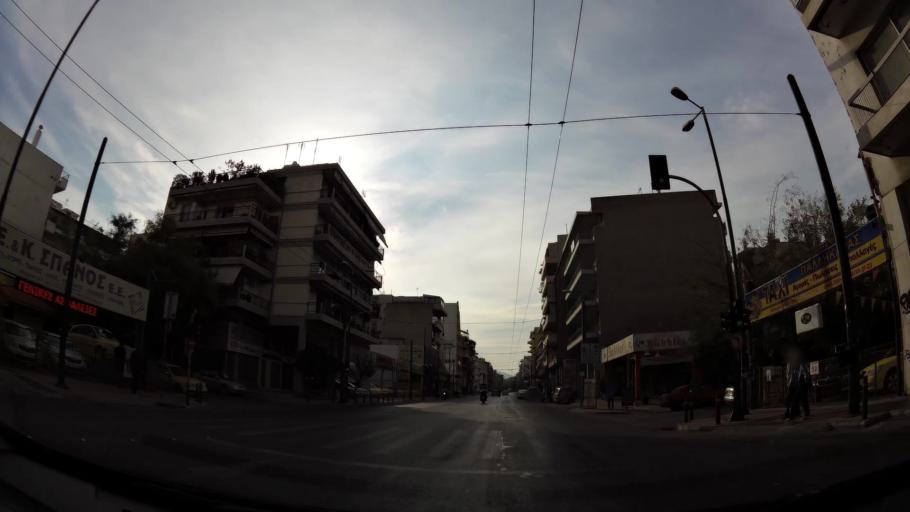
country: GR
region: Attica
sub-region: Nomarchia Athinas
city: Athens
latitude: 37.9904
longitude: 23.7157
